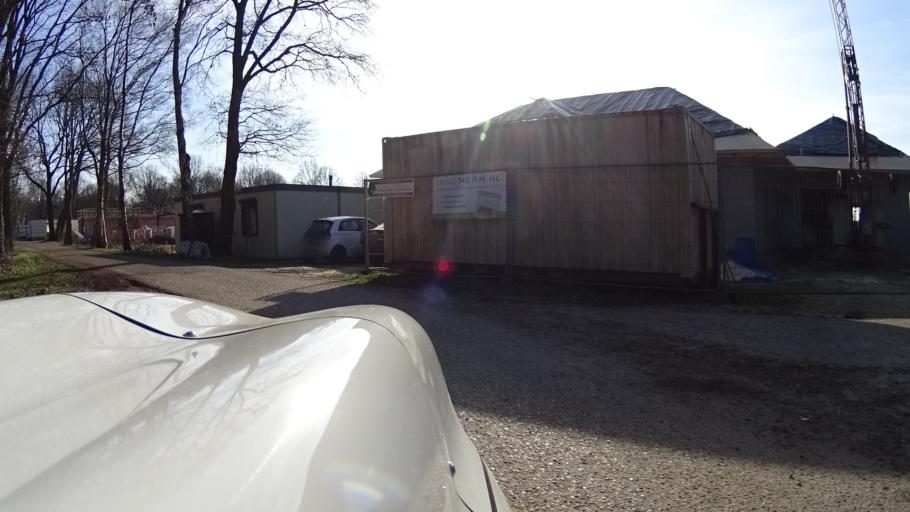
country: NL
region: North Brabant
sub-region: Gemeente Boekel
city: Boekel
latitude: 51.5912
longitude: 5.7103
